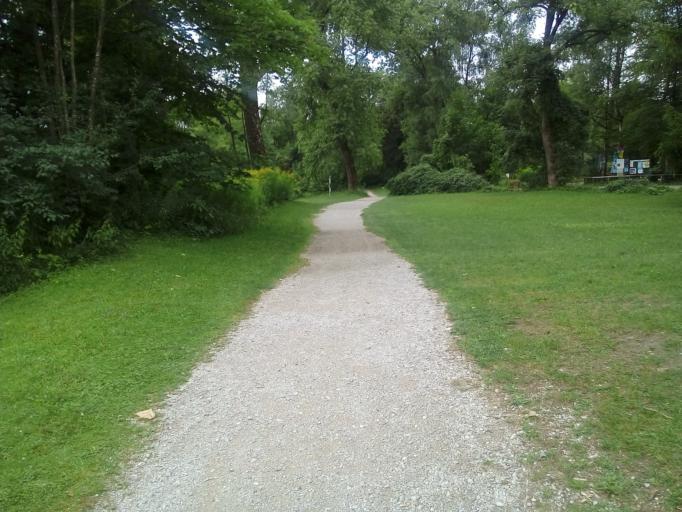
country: DE
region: Bavaria
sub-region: Upper Bavaria
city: Unterfoehring
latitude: 48.2013
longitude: 11.6423
